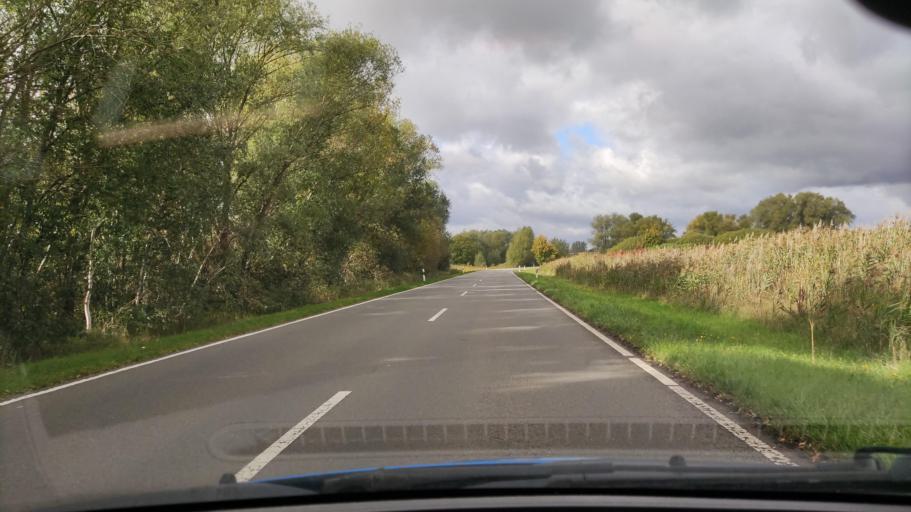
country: DE
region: Saxony-Anhalt
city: Salzwedel
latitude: 52.8559
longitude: 11.1795
